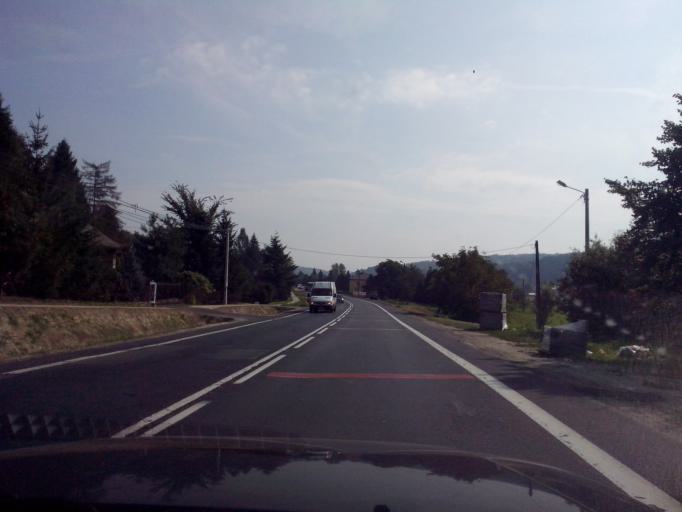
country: PL
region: Subcarpathian Voivodeship
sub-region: Powiat strzyzowski
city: Babica
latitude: 49.9356
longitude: 21.8883
